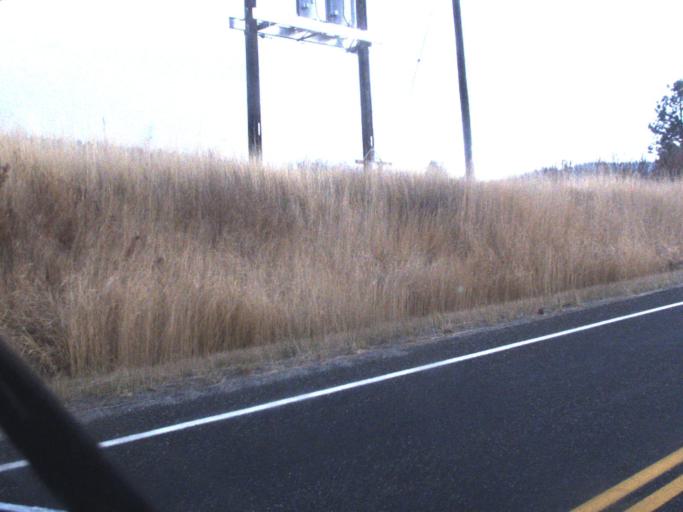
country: US
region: Washington
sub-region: Stevens County
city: Kettle Falls
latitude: 48.4497
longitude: -118.1718
